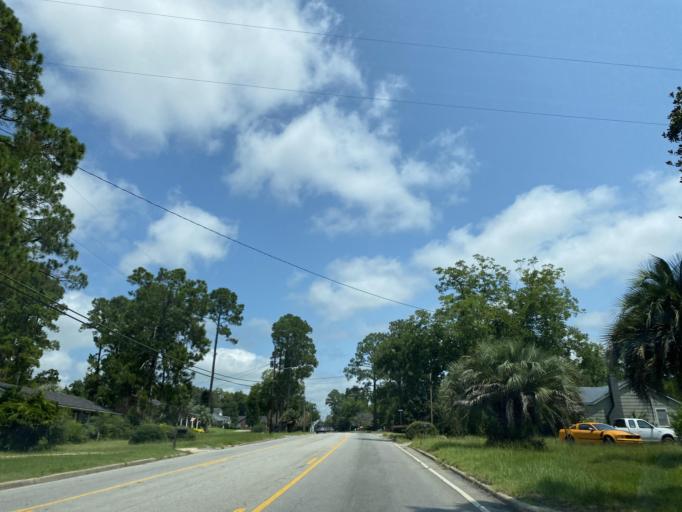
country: US
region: Georgia
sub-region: Telfair County
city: McRae
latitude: 32.0596
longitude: -82.9038
